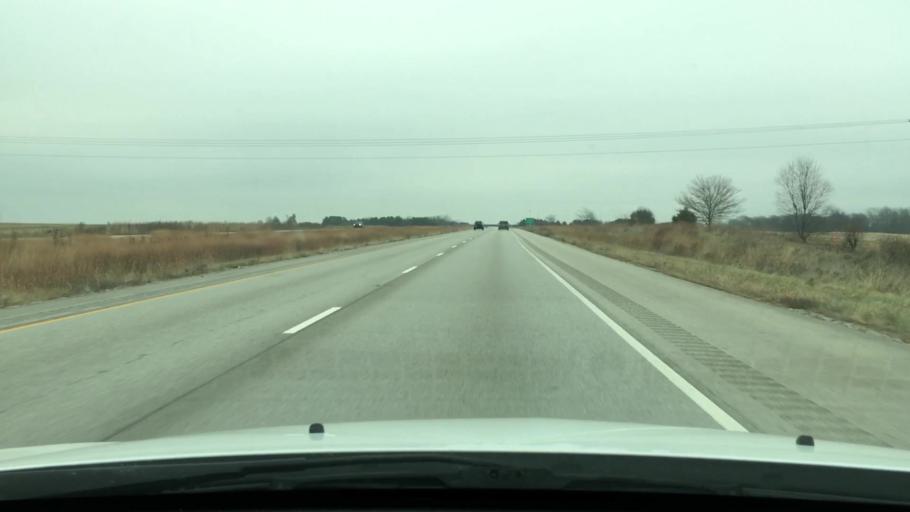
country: US
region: Illinois
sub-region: Sangamon County
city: New Berlin
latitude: 39.7367
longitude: -90.0544
